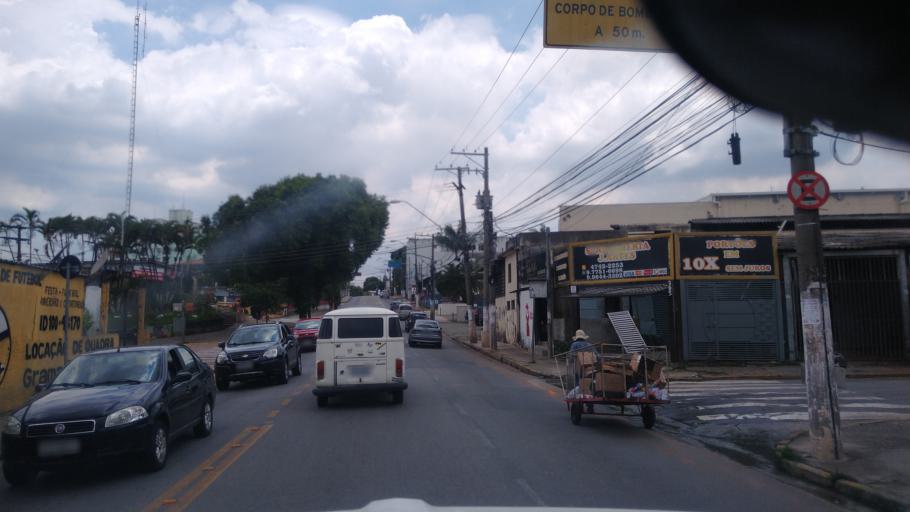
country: BR
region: Sao Paulo
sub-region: Suzano
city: Suzano
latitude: -23.5525
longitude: -46.3191
